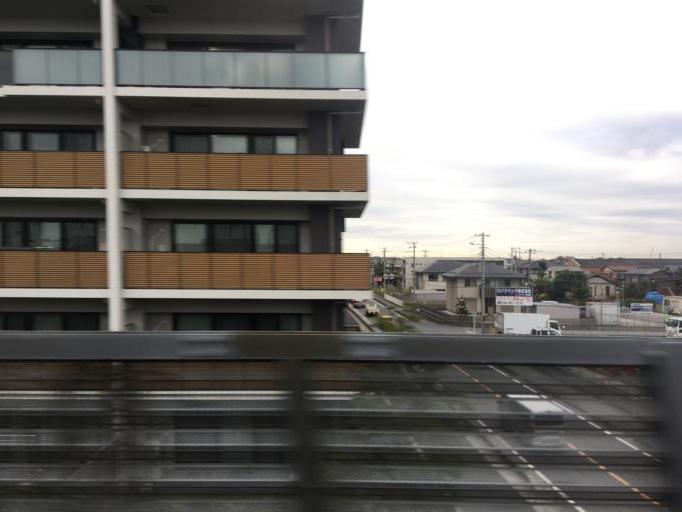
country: JP
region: Saitama
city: Yoshikawa
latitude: 35.8764
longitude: 139.8305
